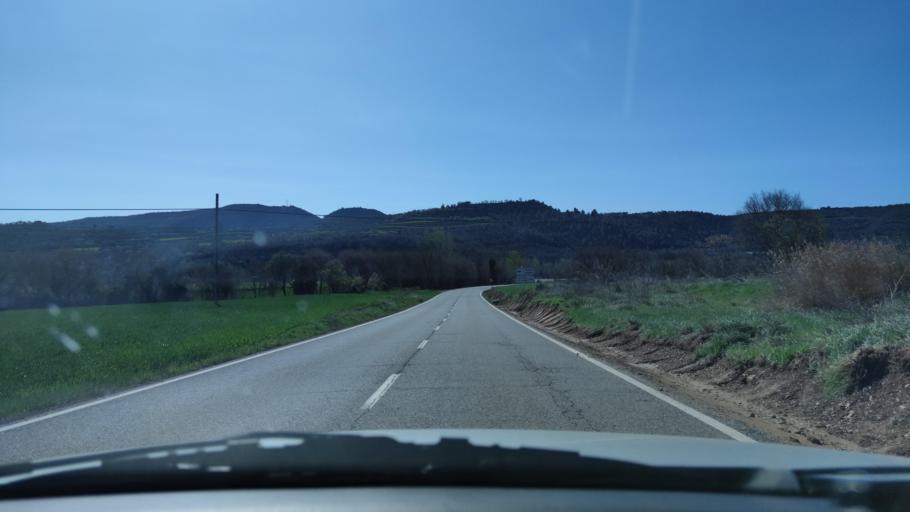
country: ES
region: Catalonia
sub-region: Provincia de Lleida
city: Artesa de Segre
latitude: 41.9218
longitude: 1.0724
